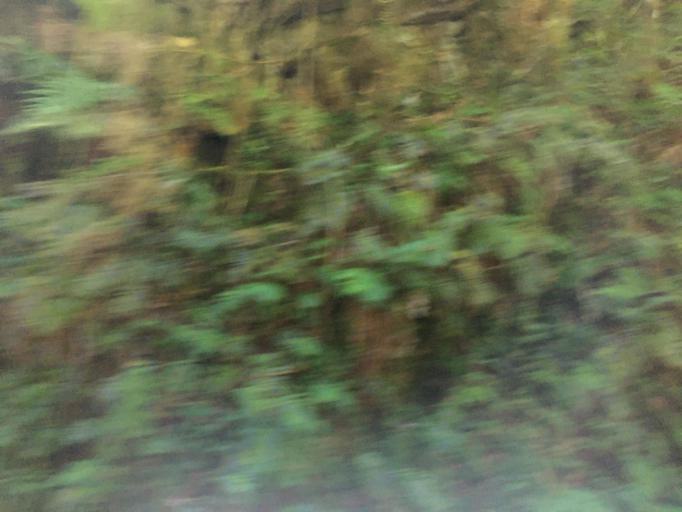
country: TW
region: Taiwan
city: Daxi
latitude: 24.5892
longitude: 121.4104
